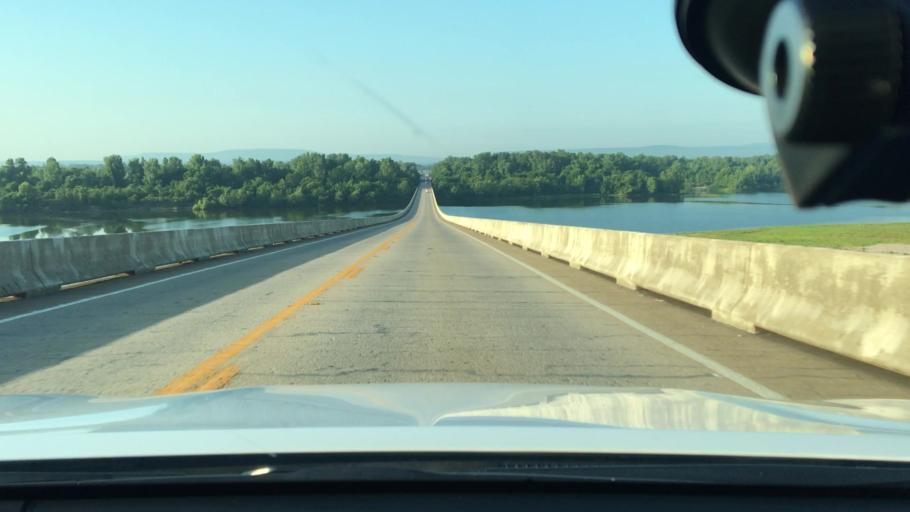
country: US
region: Arkansas
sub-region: Johnson County
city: Clarksville
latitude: 35.4099
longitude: -93.5320
